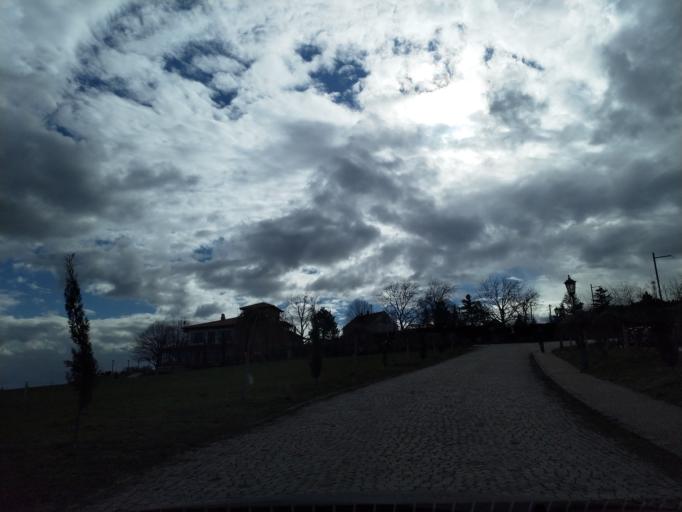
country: RS
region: Central Serbia
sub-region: Belgrade
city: Grocka
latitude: 44.6662
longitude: 20.7218
